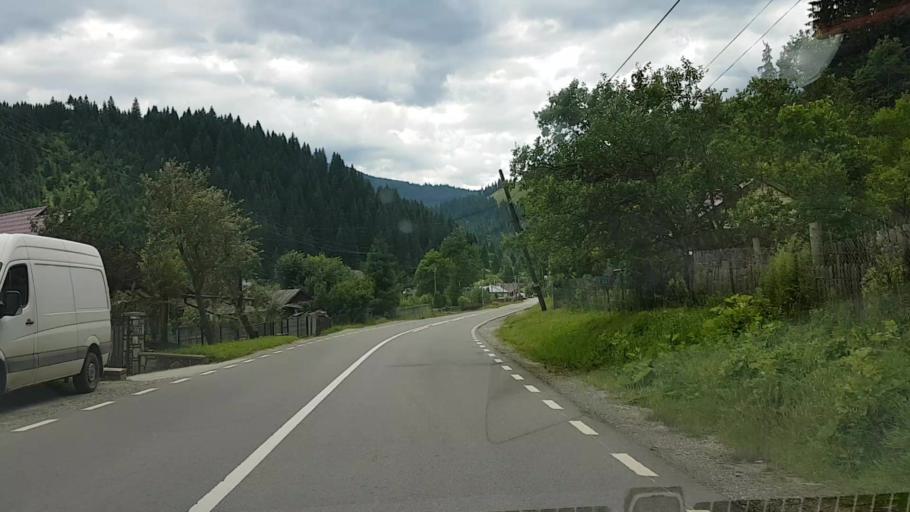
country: RO
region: Neamt
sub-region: Comuna Farcasa
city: Farcasa
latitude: 47.1492
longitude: 25.8648
